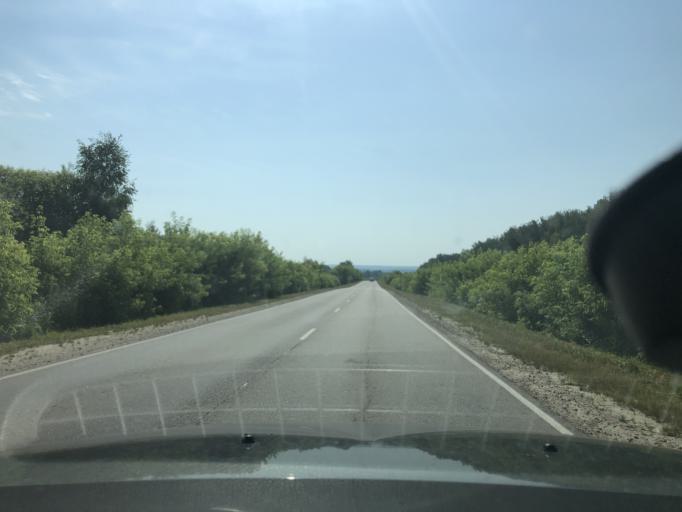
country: RU
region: Tula
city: Dubna
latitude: 54.1133
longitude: 37.0917
